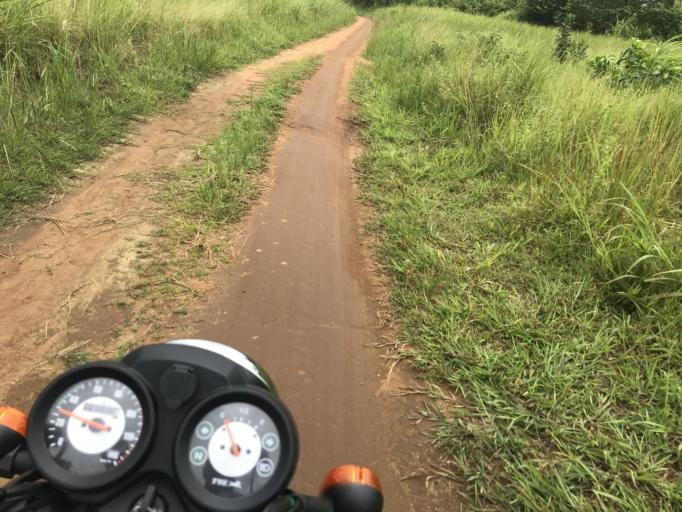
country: SL
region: Eastern Province
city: Buedu
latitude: 8.4758
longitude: -10.3167
